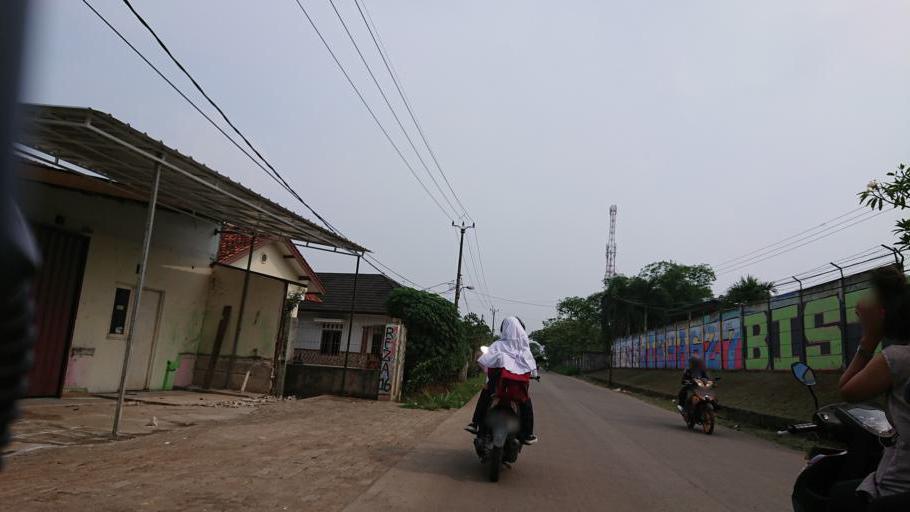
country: ID
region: West Java
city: Parung
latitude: -6.4040
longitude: 106.6921
